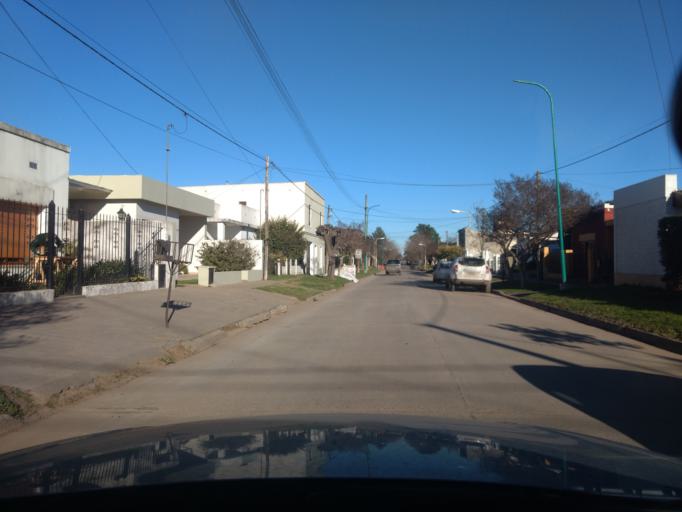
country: AR
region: Buenos Aires
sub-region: Partido de Navarro
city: Navarro
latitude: -34.9995
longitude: -59.2736
